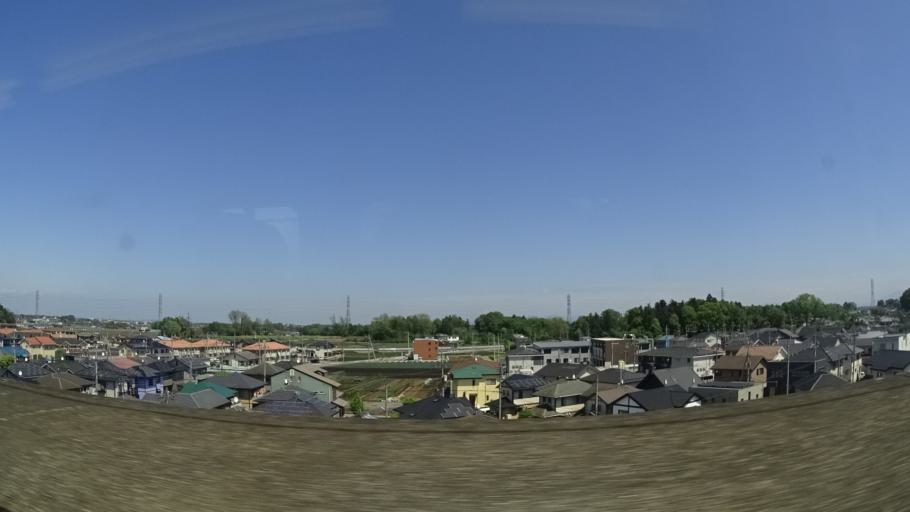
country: JP
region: Tochigi
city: Kaminokawa
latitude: 36.4774
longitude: 139.8742
